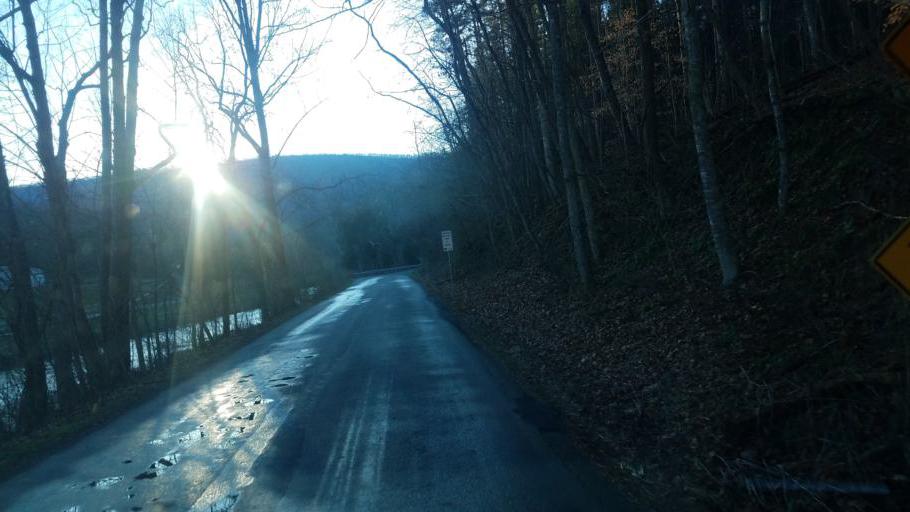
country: US
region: Virginia
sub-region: Giles County
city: Narrows
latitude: 37.1883
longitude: -80.8338
